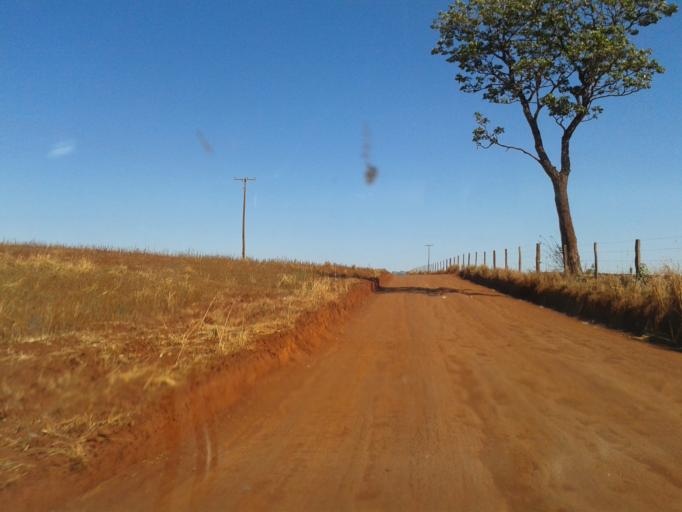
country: BR
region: Minas Gerais
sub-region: Centralina
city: Centralina
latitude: -18.5914
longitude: -49.1685
